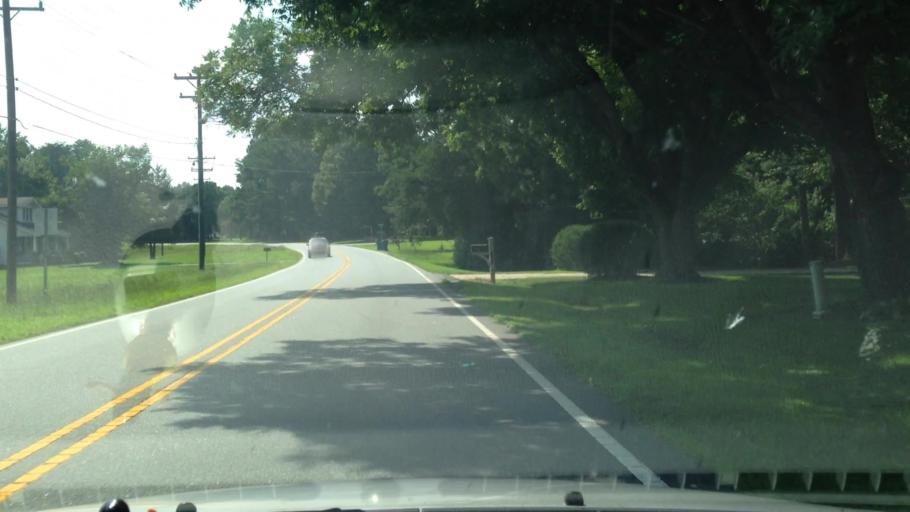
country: US
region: North Carolina
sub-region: Guilford County
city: Oak Ridge
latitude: 36.1535
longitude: -80.0319
